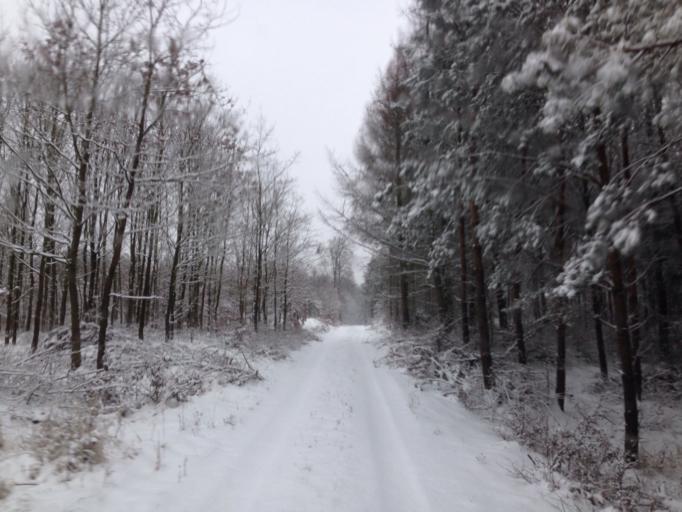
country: PL
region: Kujawsko-Pomorskie
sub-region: Powiat brodnicki
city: Gorzno
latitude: 53.1843
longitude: 19.6828
